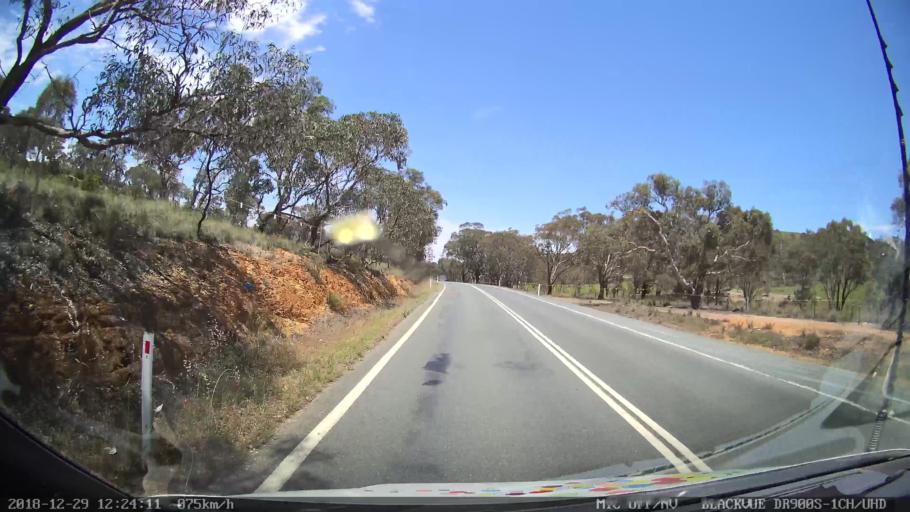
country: AU
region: New South Wales
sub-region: Queanbeyan
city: Queanbeyan
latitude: -35.4443
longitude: 149.2126
